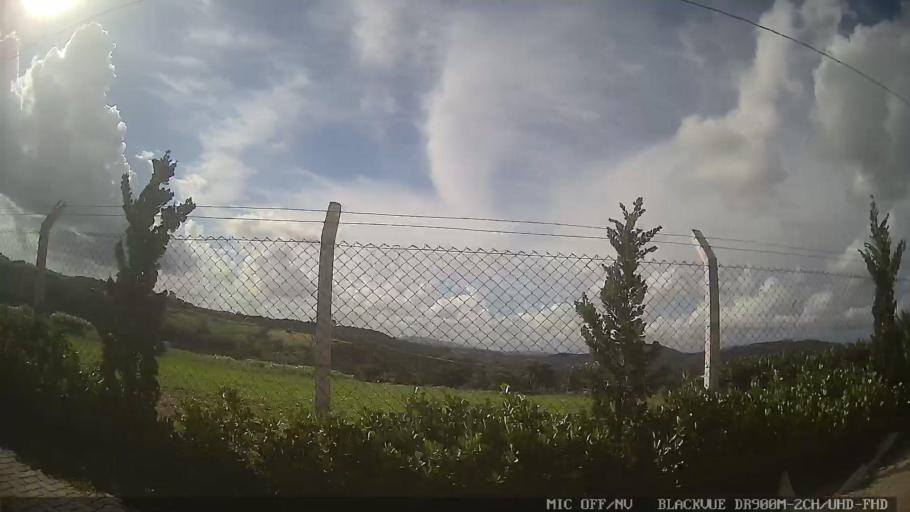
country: BR
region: Sao Paulo
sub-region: Bom Jesus Dos Perdoes
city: Bom Jesus dos Perdoes
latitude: -23.1229
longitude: -46.4899
